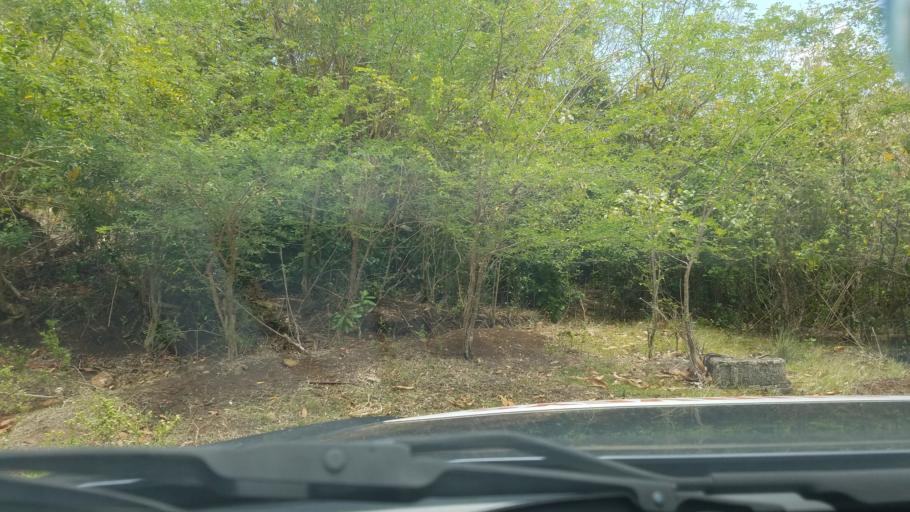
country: LC
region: Gros-Islet
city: Gros Islet
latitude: 14.0587
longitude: -60.9348
